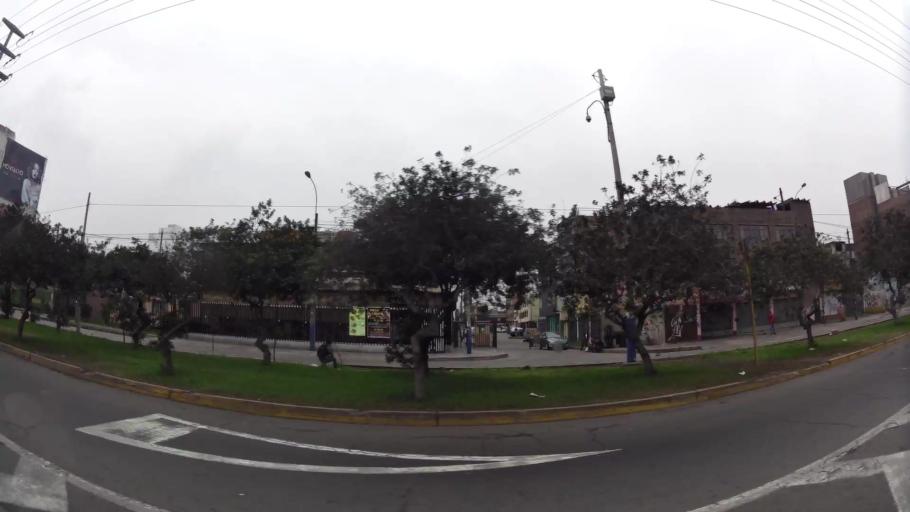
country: PE
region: Lima
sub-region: Lima
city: San Luis
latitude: -12.0824
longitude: -76.9852
